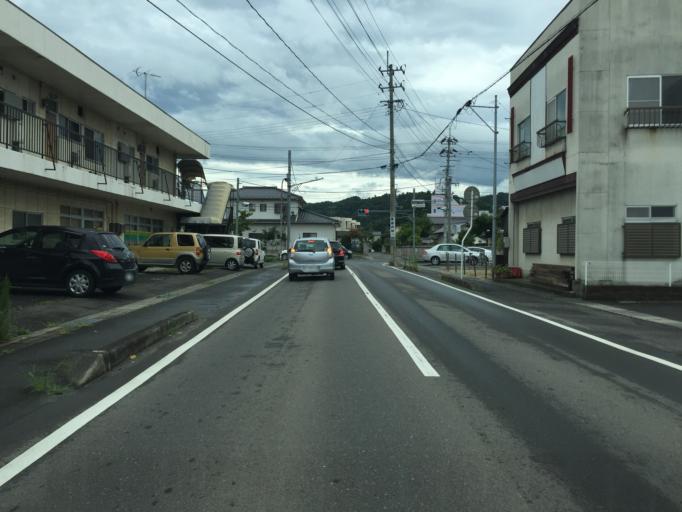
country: JP
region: Fukushima
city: Fukushima-shi
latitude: 37.7272
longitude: 140.4712
